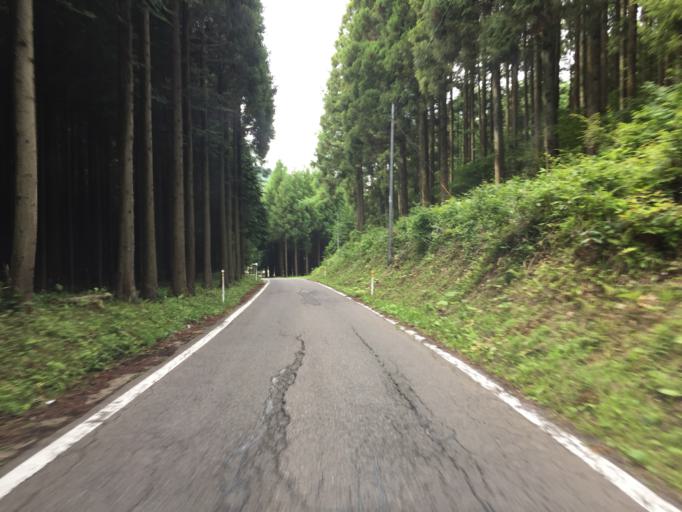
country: JP
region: Fukushima
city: Funehikimachi-funehiki
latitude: 37.4692
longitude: 140.6408
